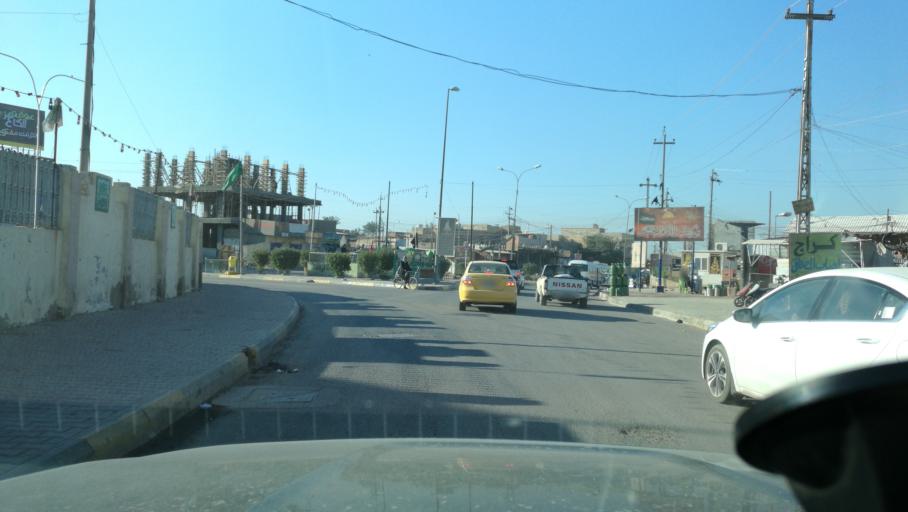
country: IQ
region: Basra Governorate
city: Al Basrah al Qadimah
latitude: 30.4941
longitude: 47.8187
